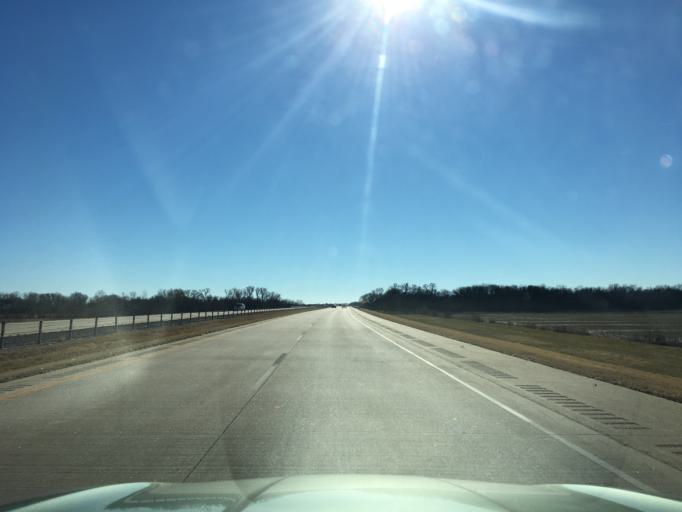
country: US
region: Oklahoma
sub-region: Noble County
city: Perry
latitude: 36.4812
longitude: -97.3272
